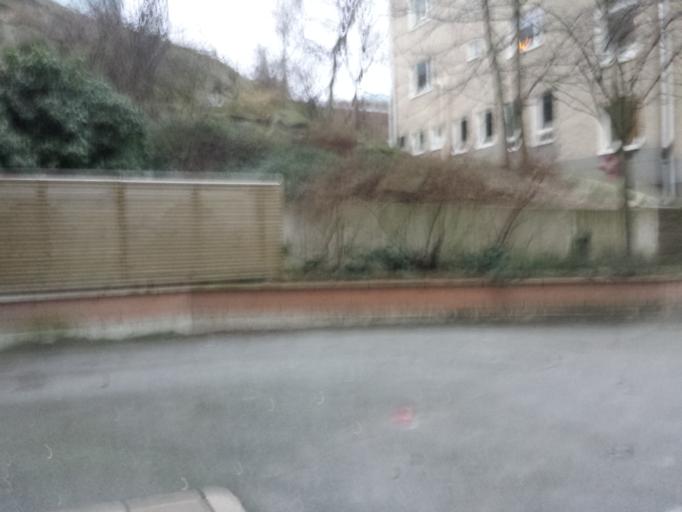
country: SE
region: Stockholm
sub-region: Solna Kommun
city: Solna
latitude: 59.3637
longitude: 18.0134
